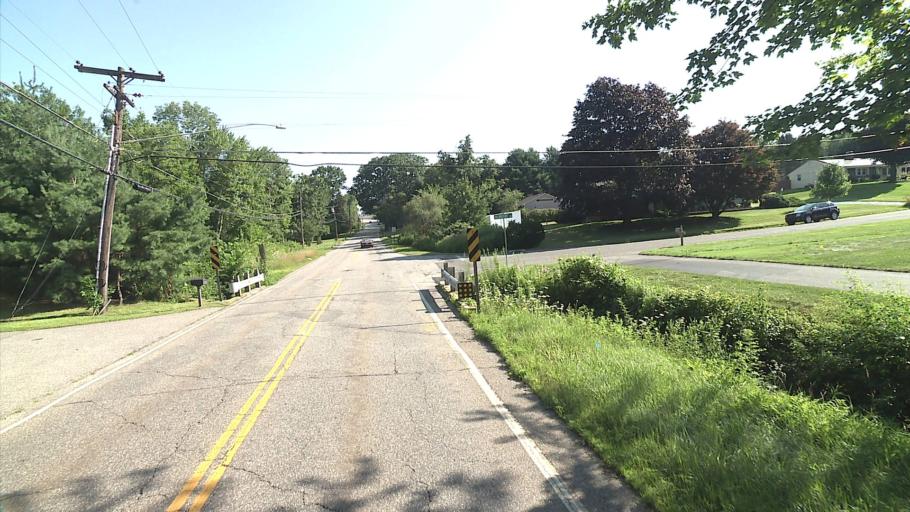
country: US
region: Connecticut
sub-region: Litchfield County
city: Northwest Harwinton
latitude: 41.8159
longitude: -73.0825
